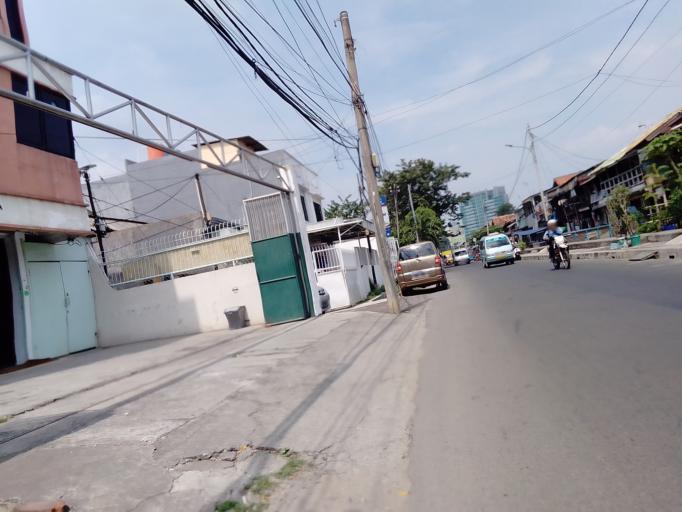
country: ID
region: Jakarta Raya
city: Jakarta
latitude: -6.1760
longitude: 106.8080
